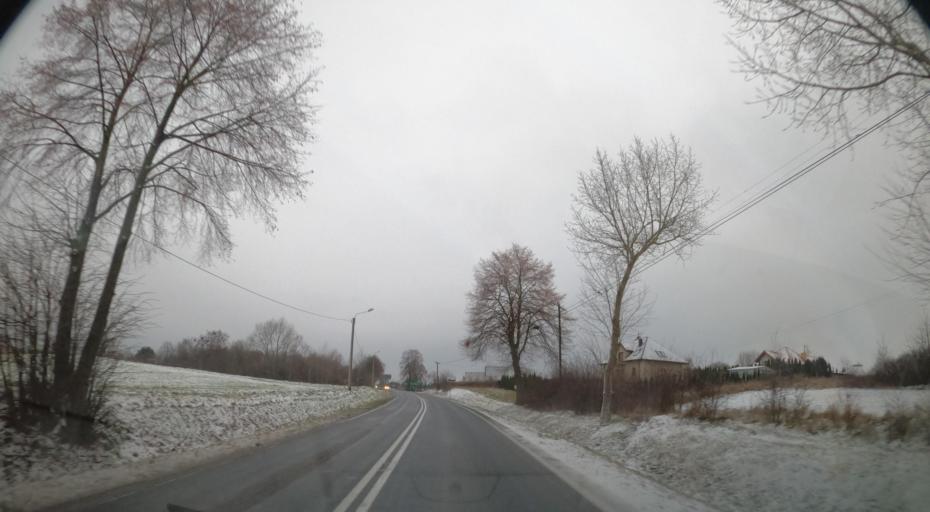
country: PL
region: Masovian Voivodeship
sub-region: Powiat plocki
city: Maszewo Duze
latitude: 52.5706
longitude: 19.6132
